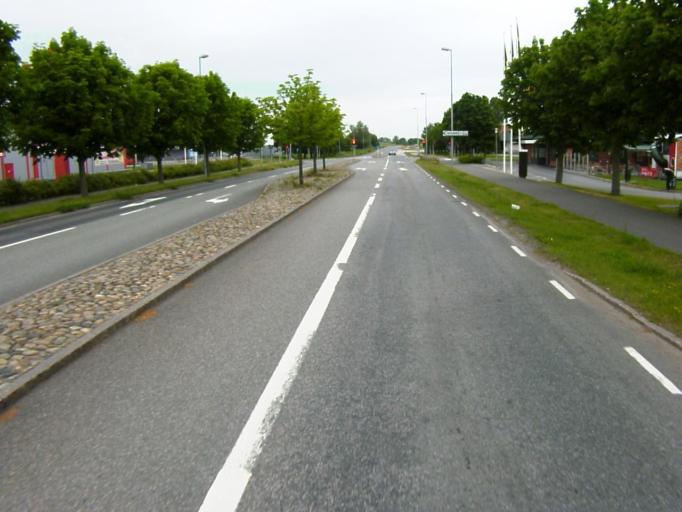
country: SE
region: Skane
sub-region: Kristianstads Kommun
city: Kristianstad
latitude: 56.0227
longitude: 14.1435
